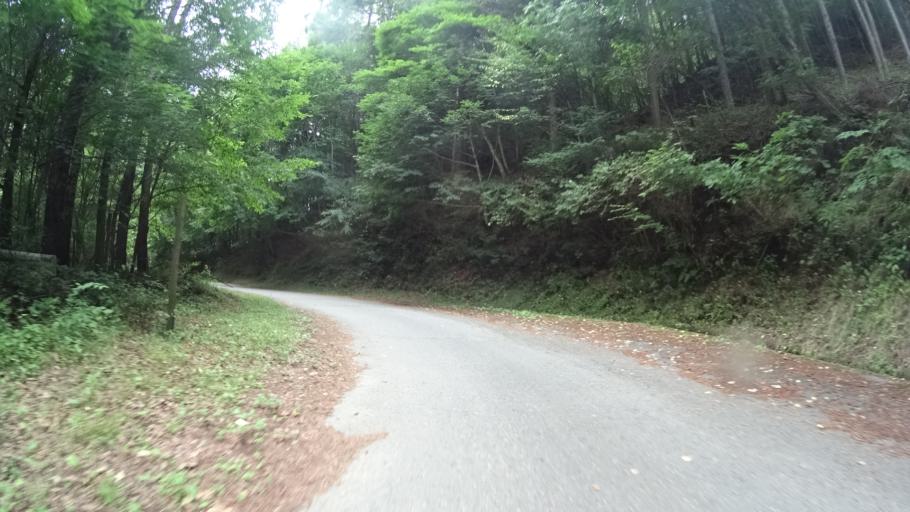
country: JP
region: Yamanashi
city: Kofu-shi
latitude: 35.8182
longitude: 138.5991
